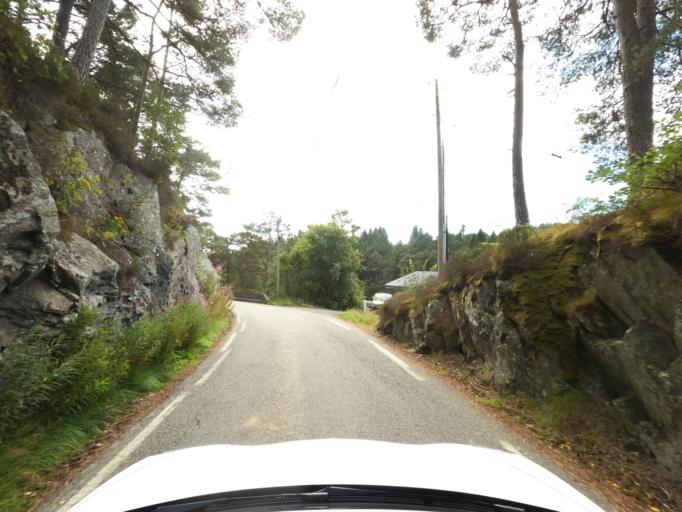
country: NO
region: Hordaland
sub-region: Os
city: Hagavik
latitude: 60.1920
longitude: 5.3532
